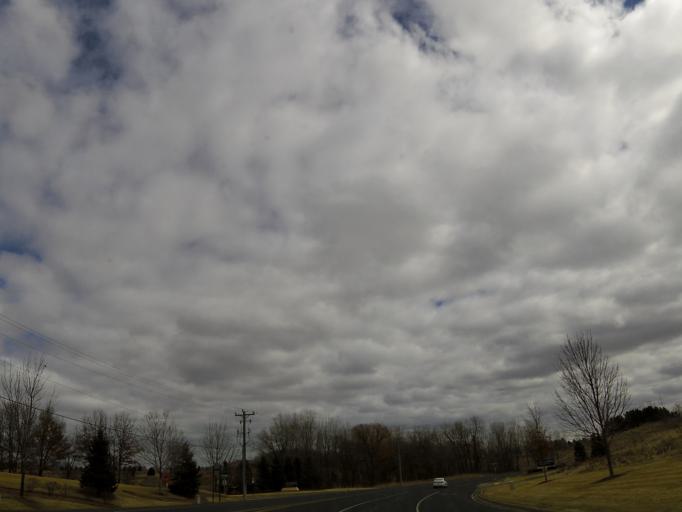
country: US
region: Minnesota
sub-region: Washington County
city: Oakdale
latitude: 44.9525
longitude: -92.9309
